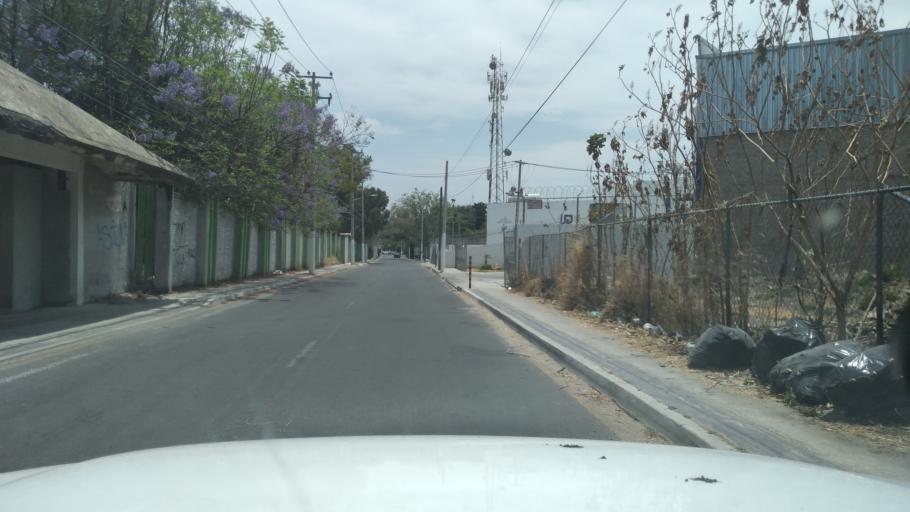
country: MX
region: Jalisco
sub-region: Zapopan
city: Zapopan
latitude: 20.7342
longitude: -103.3727
